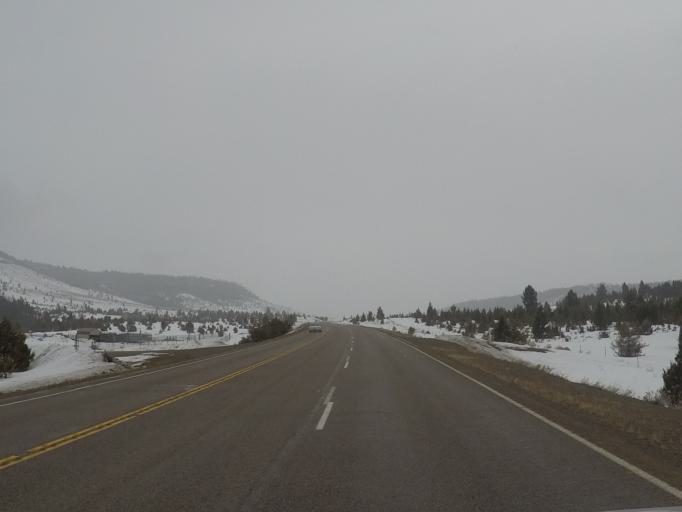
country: US
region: Montana
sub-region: Meagher County
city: White Sulphur Springs
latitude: 46.6675
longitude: -110.8771
